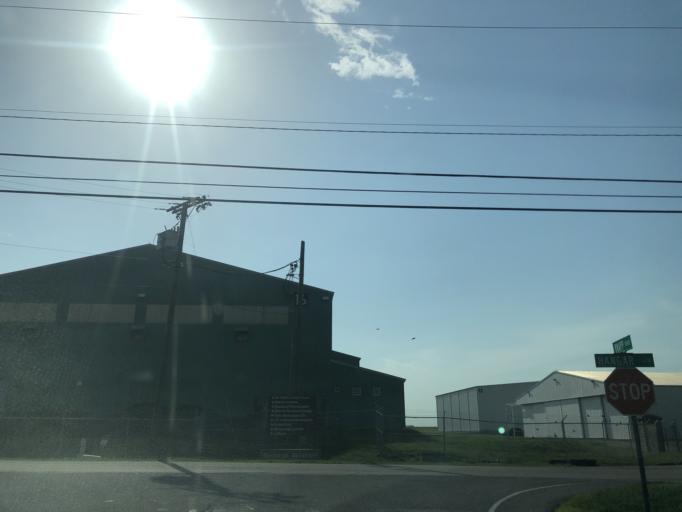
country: US
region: Tennessee
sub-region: Davidson County
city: Oak Hill
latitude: 36.1146
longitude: -86.6775
